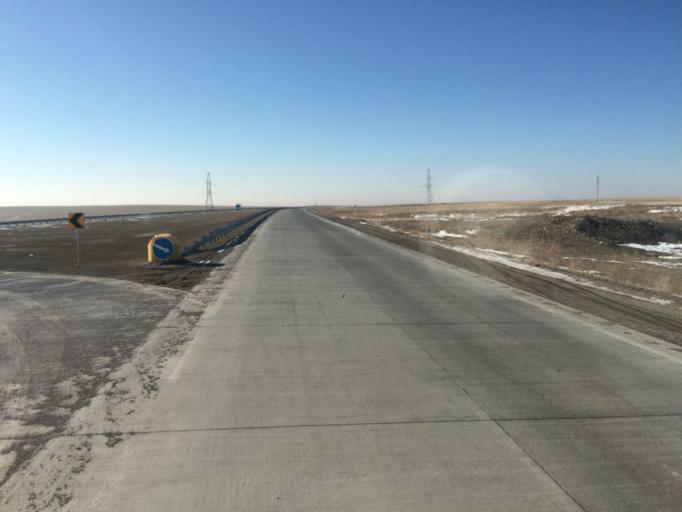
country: KZ
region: Zhambyl
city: Georgiyevka
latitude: 43.3506
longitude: 74.5474
